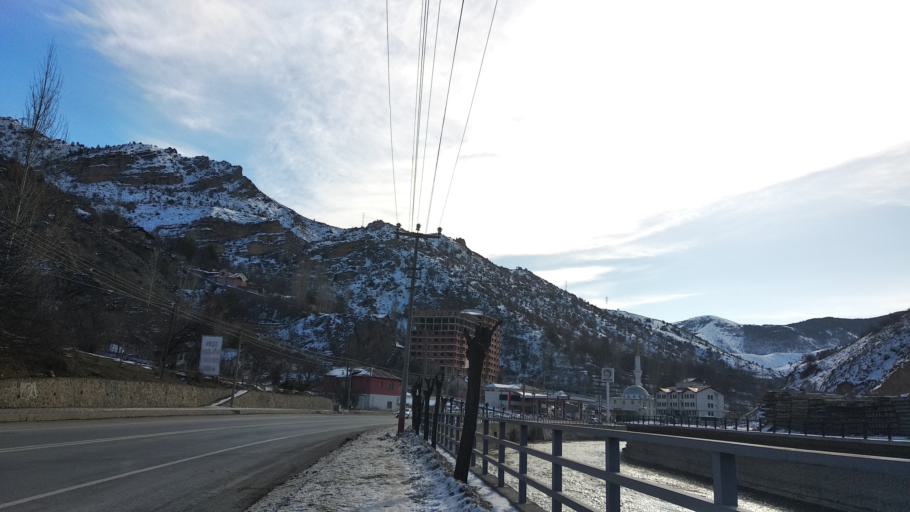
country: TR
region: Gumushane
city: Gumushkhane
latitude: 40.4466
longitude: 39.5022
